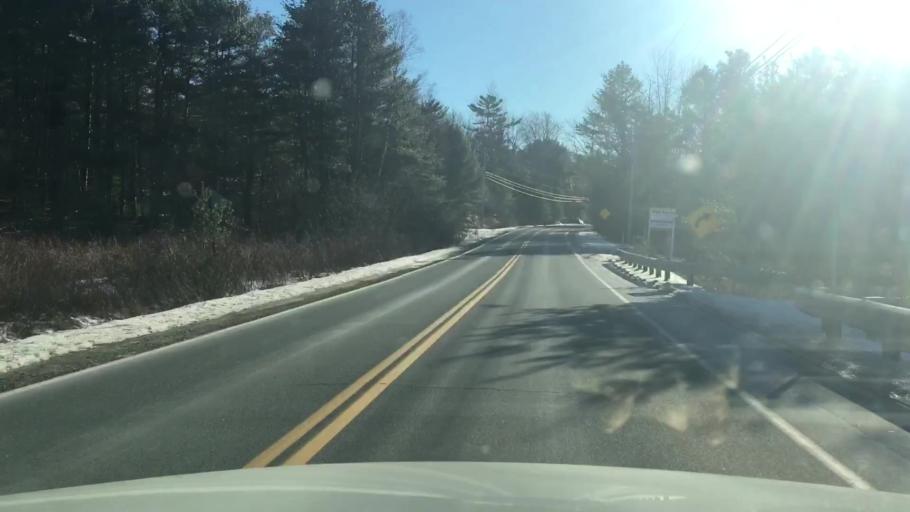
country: US
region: Maine
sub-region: Hancock County
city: Orland
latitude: 44.5465
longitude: -68.7431
